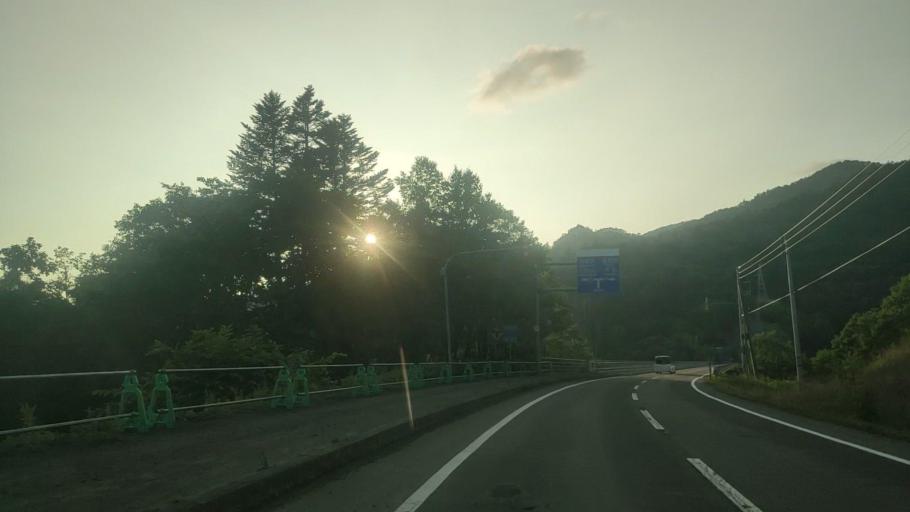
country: JP
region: Hokkaido
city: Bibai
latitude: 43.2432
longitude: 142.0231
